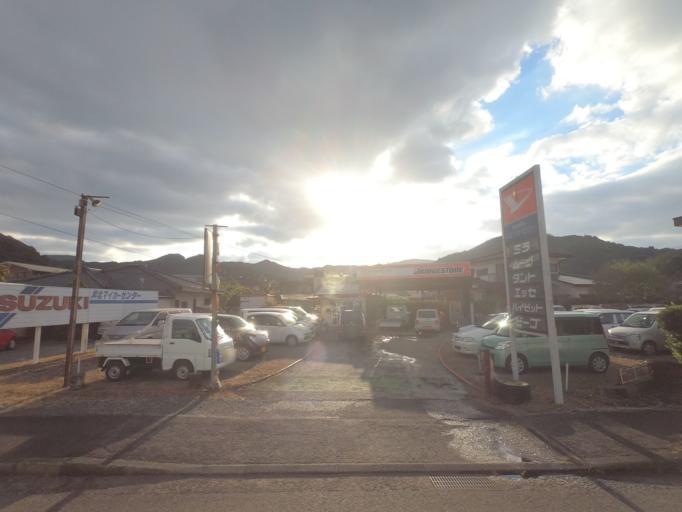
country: JP
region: Kumamoto
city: Minamata
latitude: 32.2701
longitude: 130.5032
